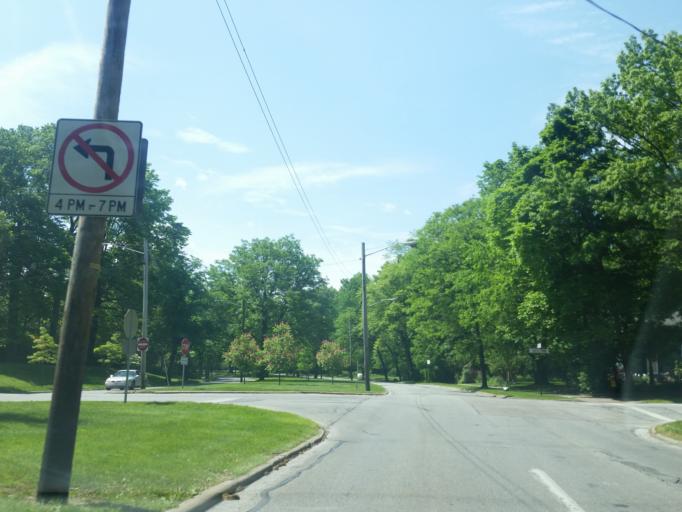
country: US
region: Ohio
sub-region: Cuyahoga County
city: Cleveland Heights
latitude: 41.4894
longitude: -81.5840
